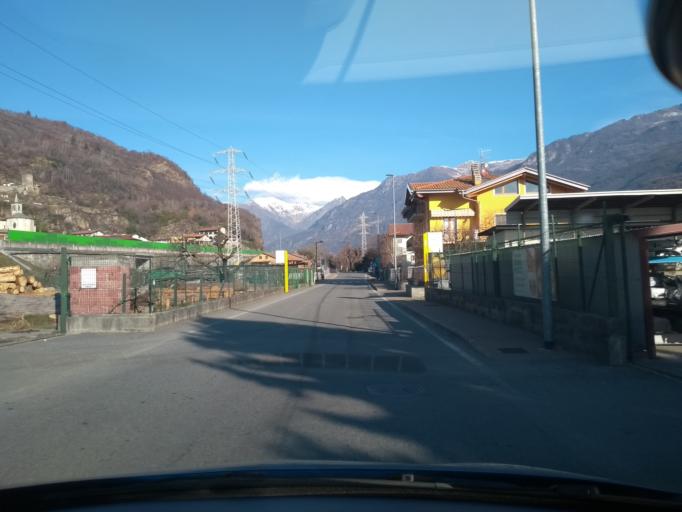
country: IT
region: Piedmont
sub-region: Provincia di Torino
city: Quassolo
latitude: 45.5229
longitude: 7.8353
